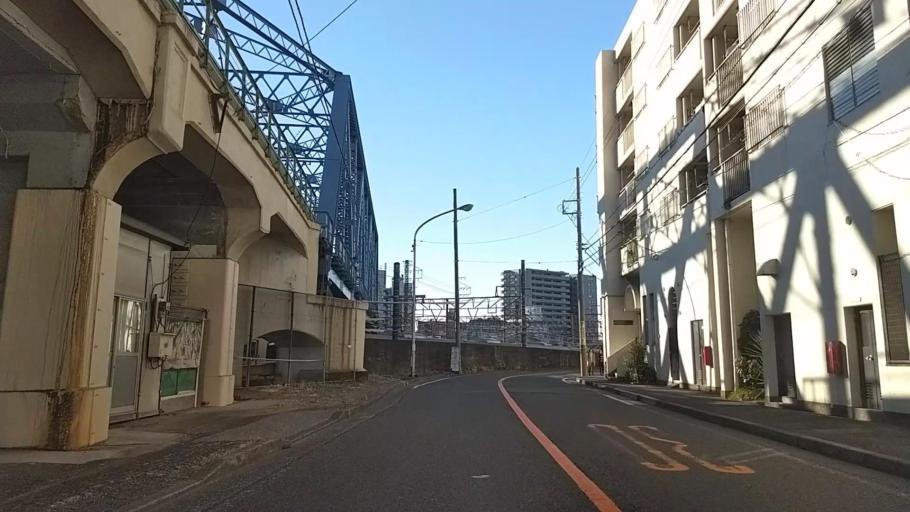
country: JP
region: Kanagawa
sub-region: Kawasaki-shi
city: Kawasaki
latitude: 35.5036
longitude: 139.6746
